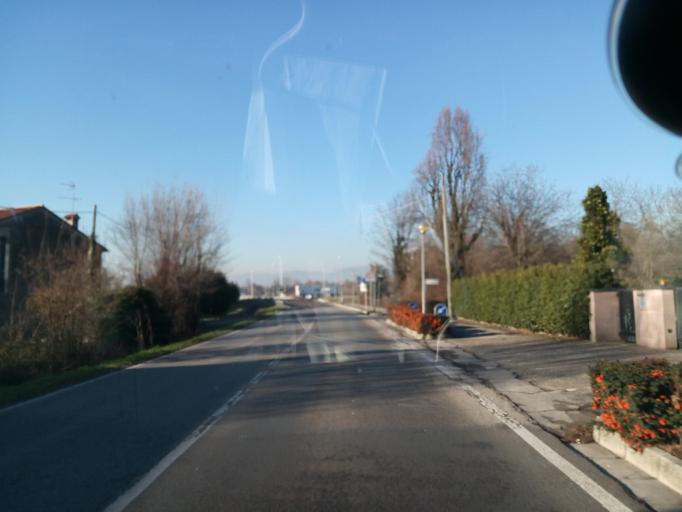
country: IT
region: Veneto
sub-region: Provincia di Treviso
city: Castelfranco Veneto
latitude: 45.6749
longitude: 11.9147
